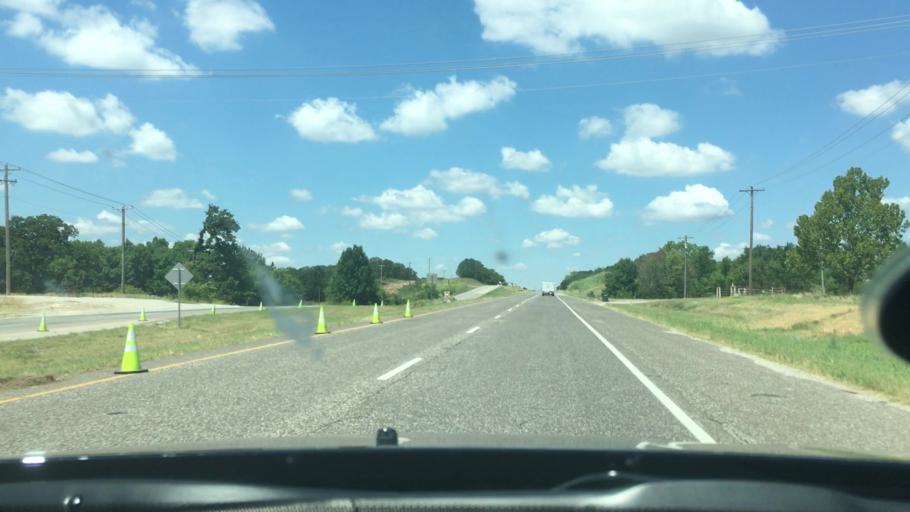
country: US
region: Oklahoma
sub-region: Carter County
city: Lone Grove
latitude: 34.1730
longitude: -97.3186
